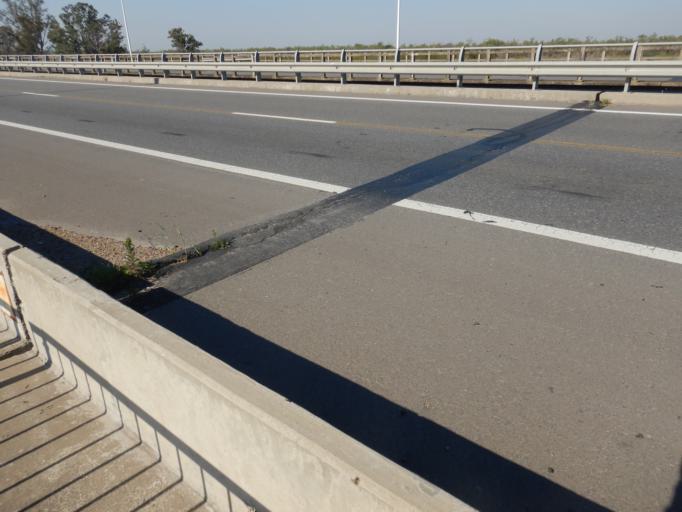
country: AR
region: Entre Rios
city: Parana
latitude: -31.6732
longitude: -60.5773
